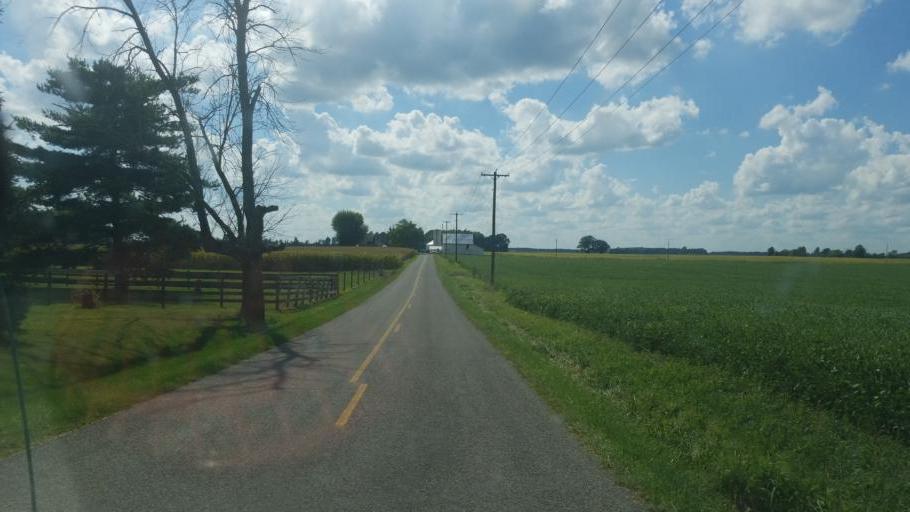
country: US
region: Ohio
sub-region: Union County
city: Richwood
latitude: 40.4336
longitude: -83.3332
